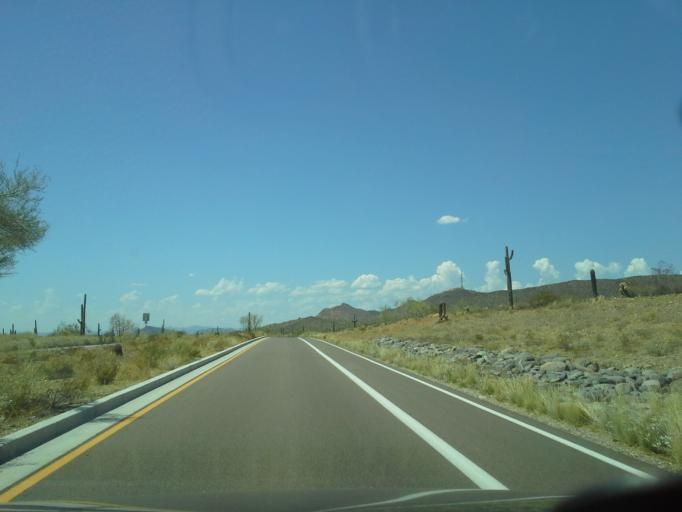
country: US
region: Arizona
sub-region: Maricopa County
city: Anthem
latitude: 33.7769
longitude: -112.0728
